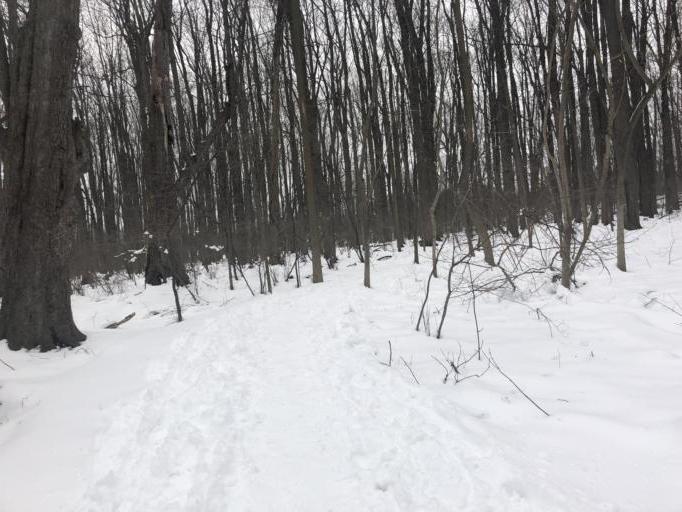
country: US
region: New York
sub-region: Monroe County
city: Pittsford
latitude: 43.0658
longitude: -77.5727
